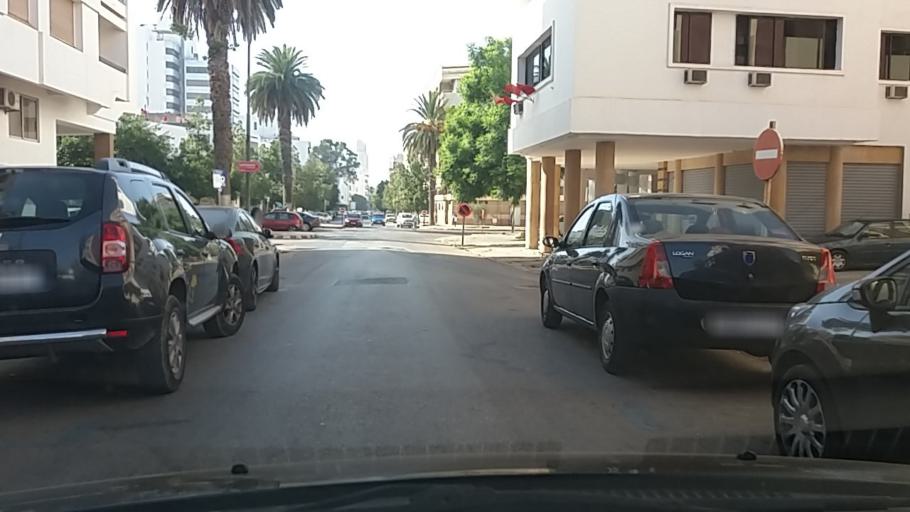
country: MA
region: Rabat-Sale-Zemmour-Zaer
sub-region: Rabat
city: Rabat
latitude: 34.0146
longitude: -6.8284
